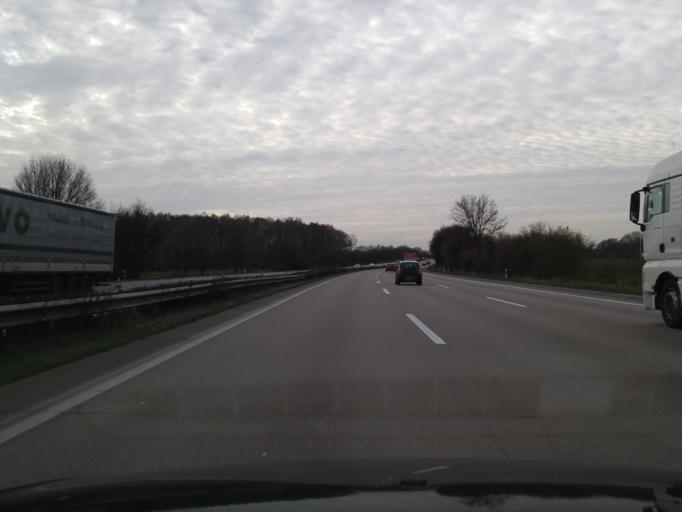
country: DE
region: Schleswig-Holstein
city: Stapelfeld
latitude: 53.6017
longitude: 10.2281
